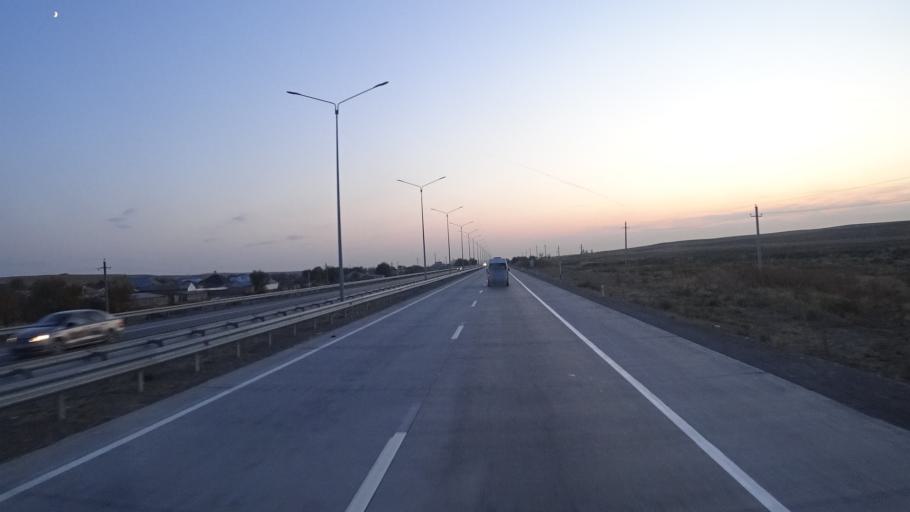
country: KZ
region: Ongtustik Qazaqstan
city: Qazyqurt
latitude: 41.8898
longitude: 69.4464
